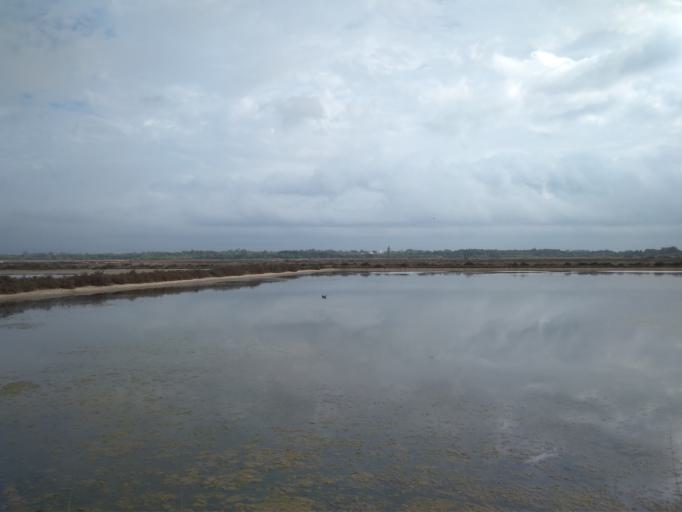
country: PT
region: Faro
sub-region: Faro
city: Faro
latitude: 37.0237
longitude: -7.9971
